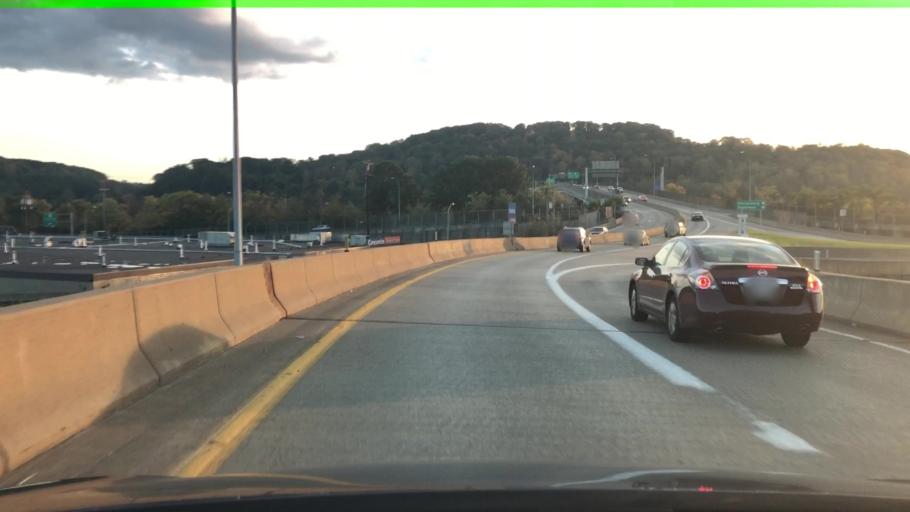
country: US
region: Pennsylvania
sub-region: Allegheny County
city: Aspinwall
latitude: 40.4938
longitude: -79.9094
